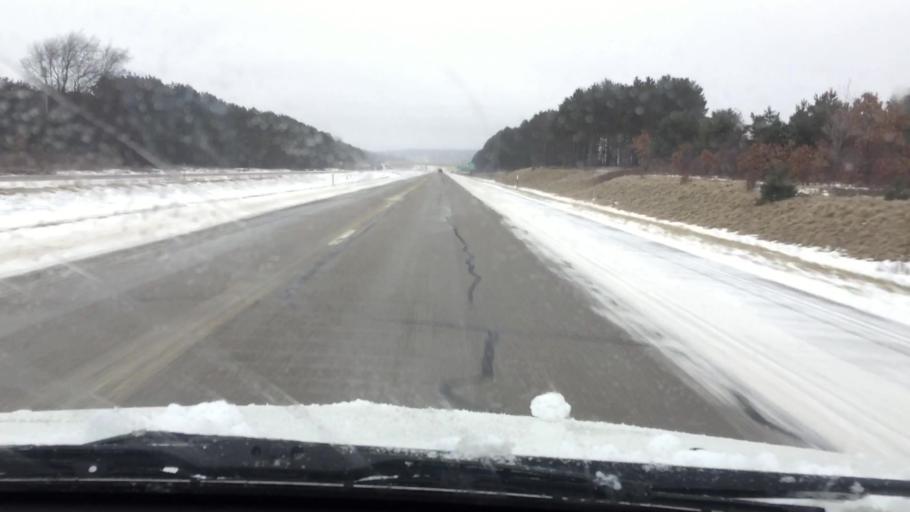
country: US
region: Michigan
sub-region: Wexford County
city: Cadillac
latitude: 44.2730
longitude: -85.3882
